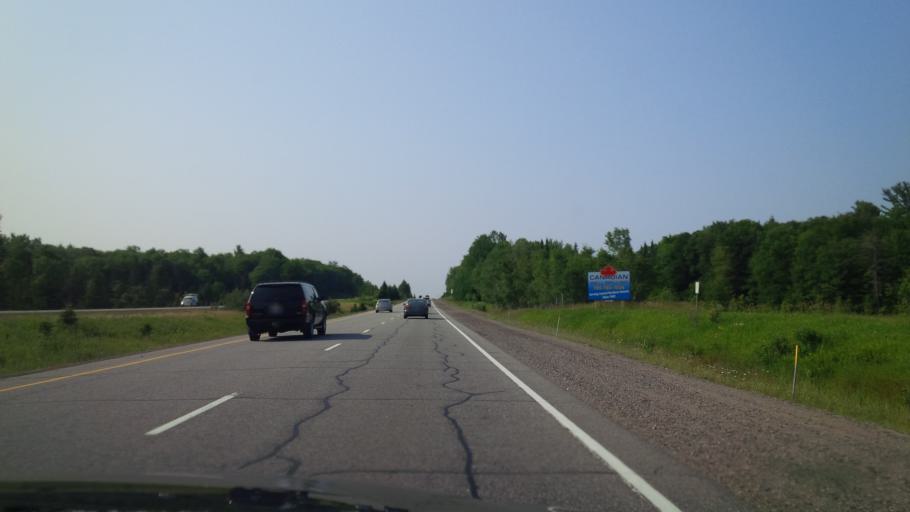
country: CA
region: Ontario
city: Bracebridge
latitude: 45.1930
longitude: -79.3136
